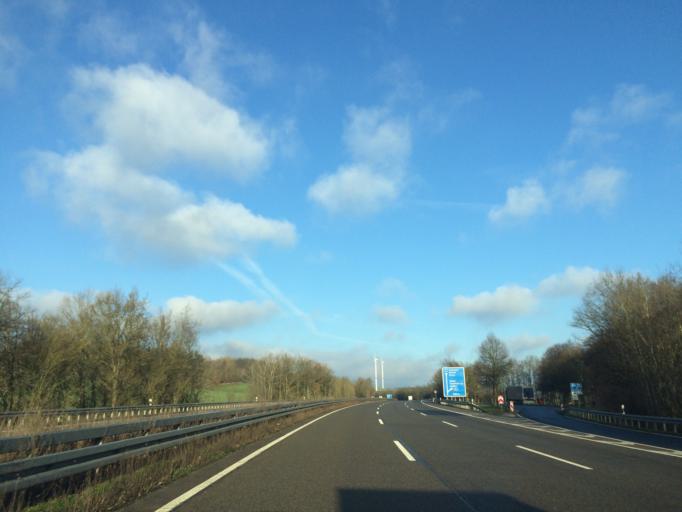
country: DE
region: Hesse
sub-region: Regierungsbezirk Kassel
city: Kirchheim
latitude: 50.7887
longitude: 9.5497
